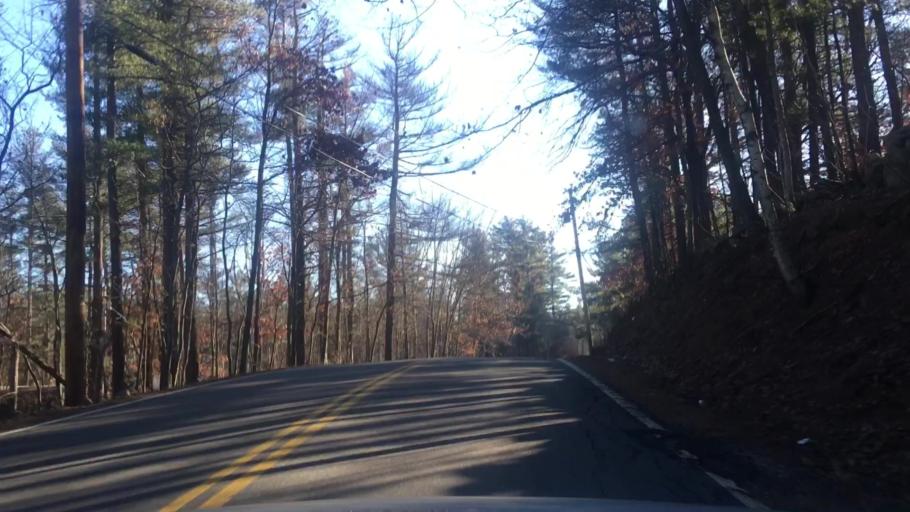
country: US
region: New Hampshire
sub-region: Rockingham County
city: Londonderry
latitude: 42.8895
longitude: -71.4093
